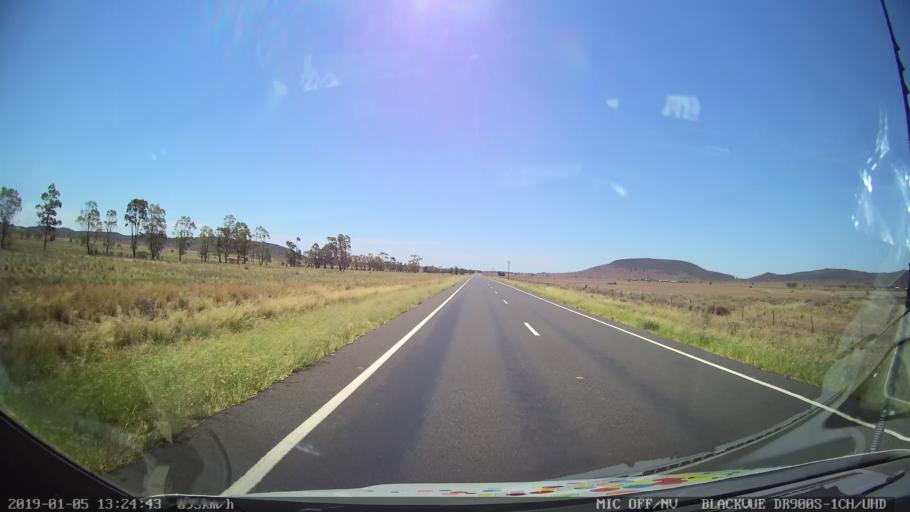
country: AU
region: New South Wales
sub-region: Gunnedah
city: Gunnedah
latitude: -31.0671
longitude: 149.9928
